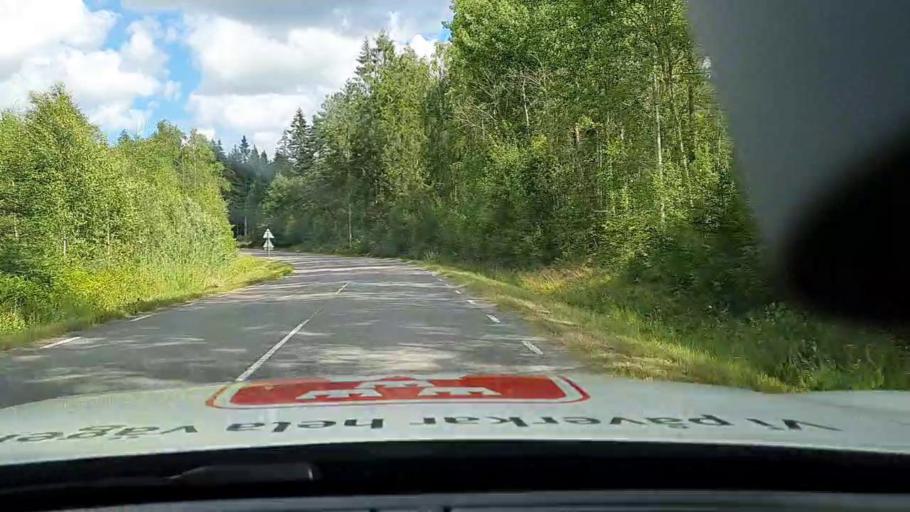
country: SE
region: Vaestra Goetaland
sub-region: Karlsborgs Kommun
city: Molltorp
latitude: 58.6057
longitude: 14.3878
